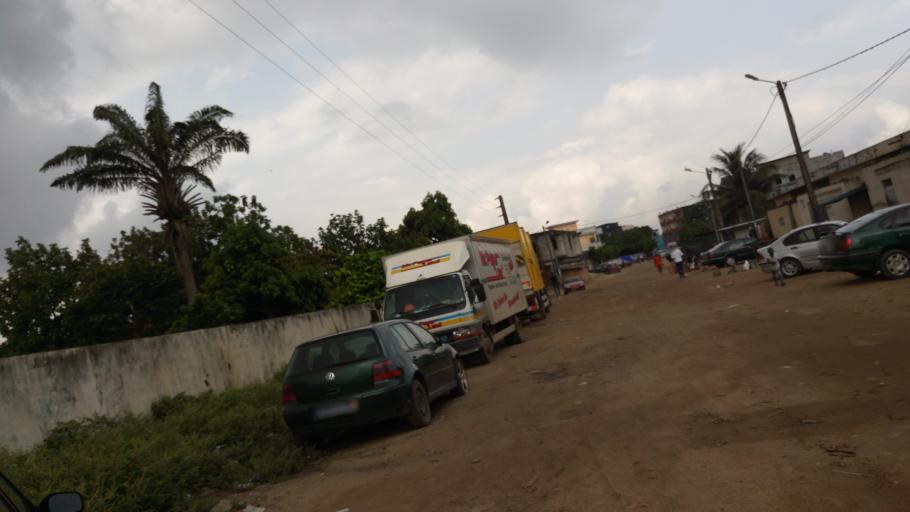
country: CI
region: Lagunes
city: Abobo
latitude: 5.4027
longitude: -4.0032
